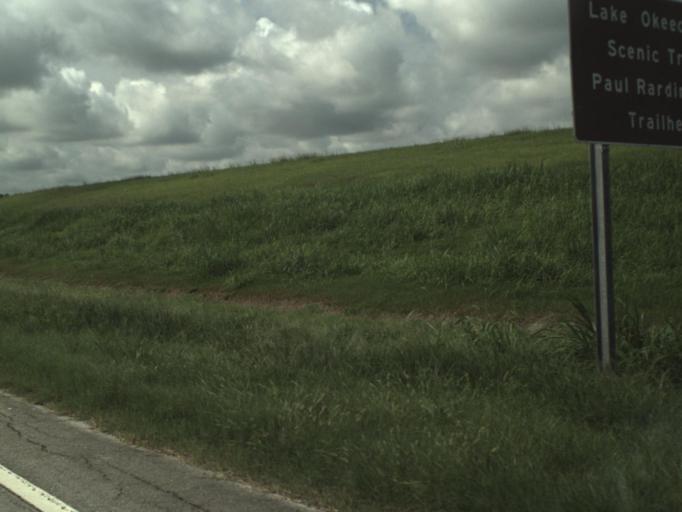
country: US
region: Florida
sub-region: Palm Beach County
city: Pahokee
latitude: 26.7534
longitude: -80.6834
